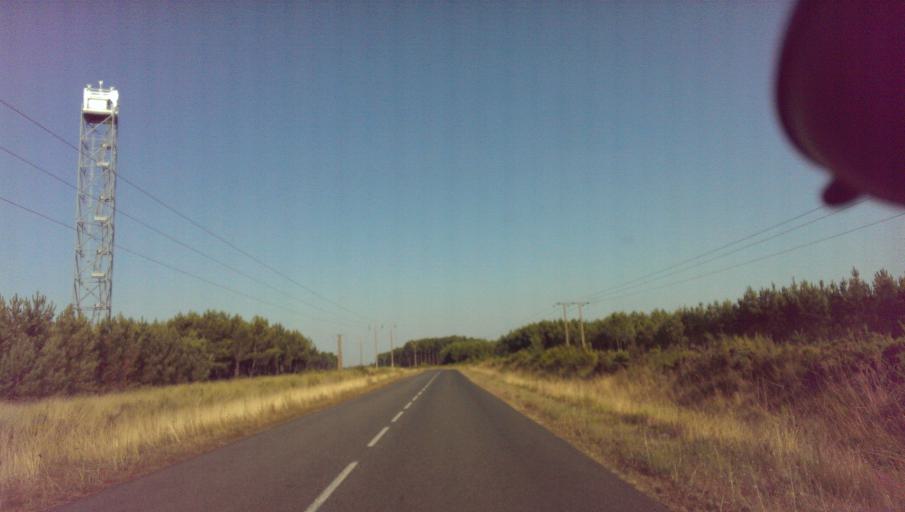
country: FR
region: Aquitaine
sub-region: Departement des Landes
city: Mimizan
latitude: 44.1800
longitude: -1.1689
